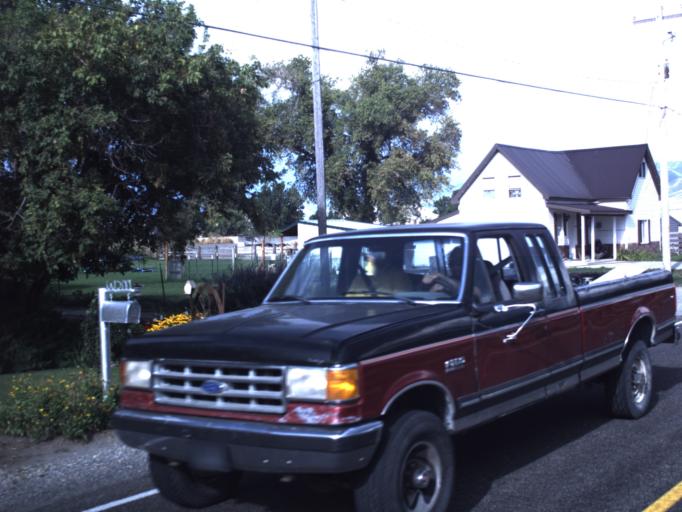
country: US
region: Utah
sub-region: Cache County
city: Lewiston
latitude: 41.9755
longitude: -111.9000
